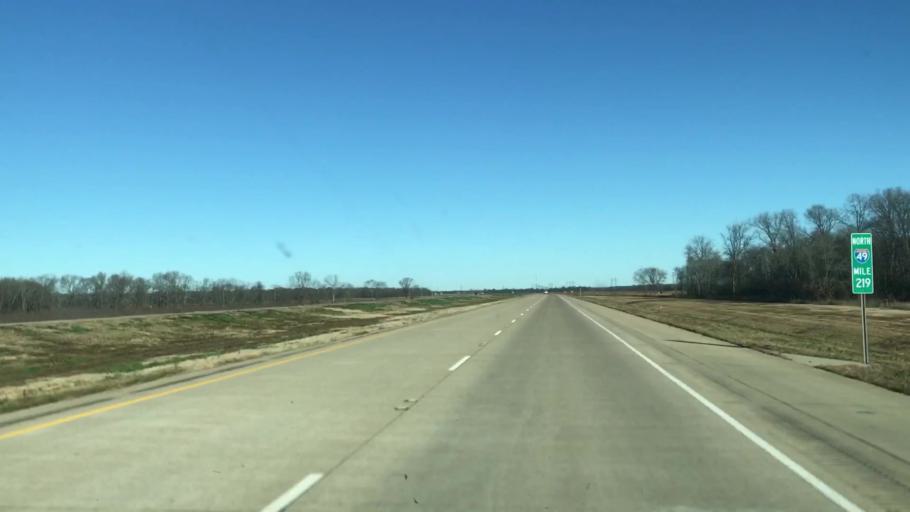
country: US
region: Louisiana
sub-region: Caddo Parish
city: Blanchard
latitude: 32.6427
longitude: -93.8391
